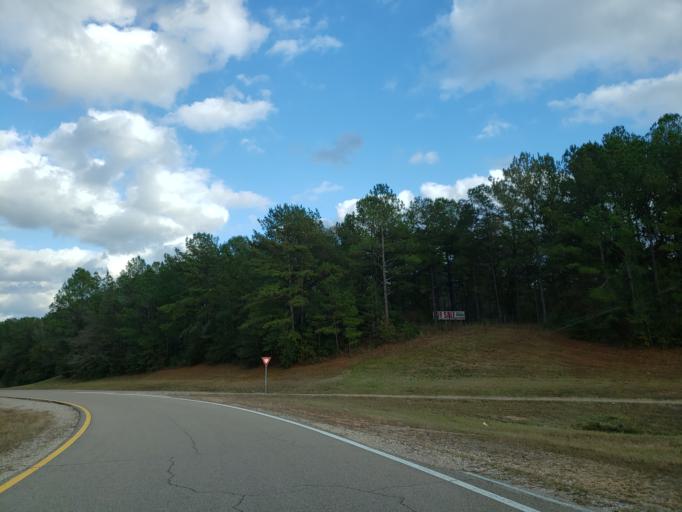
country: US
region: Mississippi
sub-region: Forrest County
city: Hattiesburg
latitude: 31.2391
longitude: -89.3018
